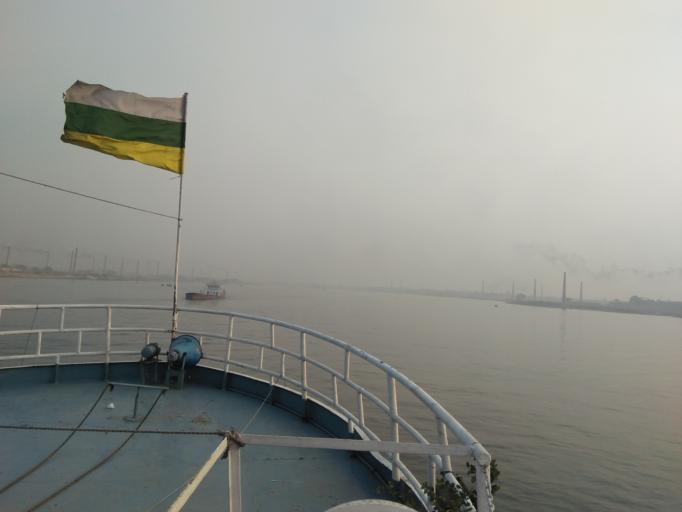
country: BD
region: Dhaka
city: Narayanganj
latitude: 23.6205
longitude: 90.4539
